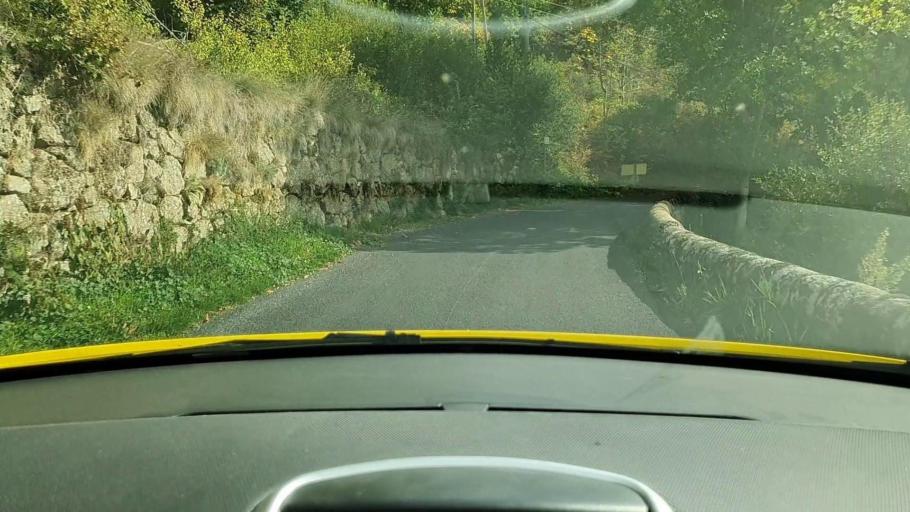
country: FR
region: Languedoc-Roussillon
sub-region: Departement de la Lozere
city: Meyrueis
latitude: 44.0705
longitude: 3.4562
